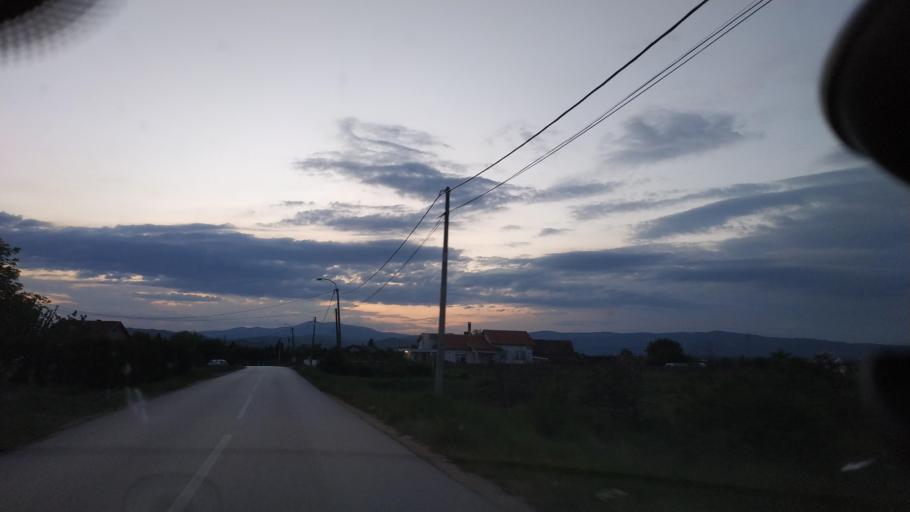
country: RS
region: Central Serbia
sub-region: Nisavski Okrug
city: Merosina
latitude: 43.2881
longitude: 21.7172
